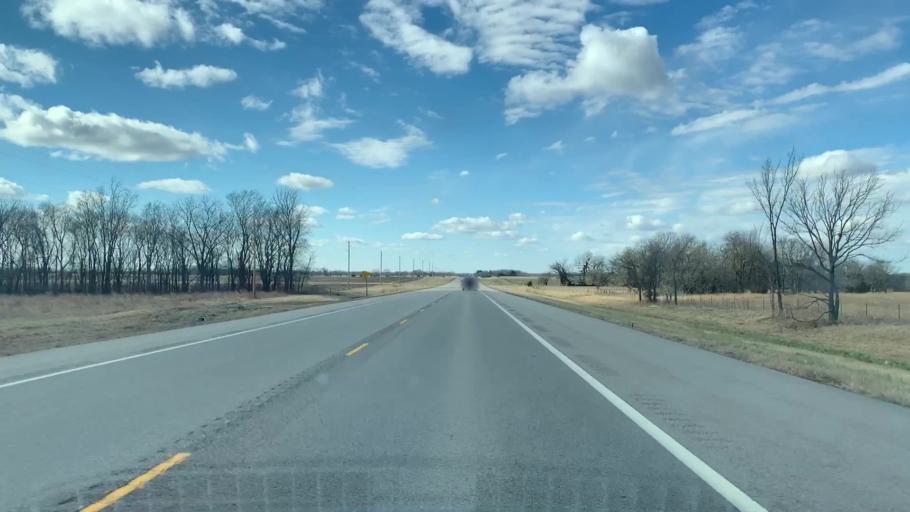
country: US
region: Kansas
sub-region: Labette County
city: Oswego
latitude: 37.3401
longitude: -95.0414
